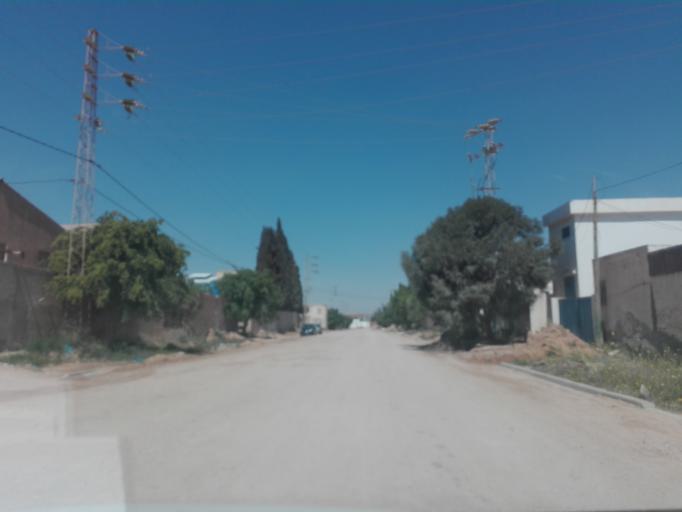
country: TN
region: Safaqis
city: Sfax
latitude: 34.7252
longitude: 10.5159
